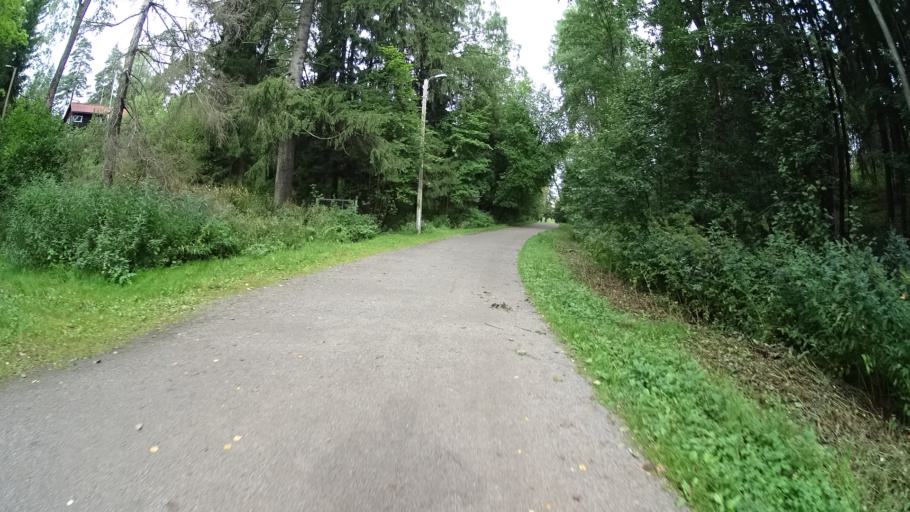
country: FI
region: Uusimaa
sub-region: Helsinki
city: Helsinki
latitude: 60.2293
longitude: 24.9820
